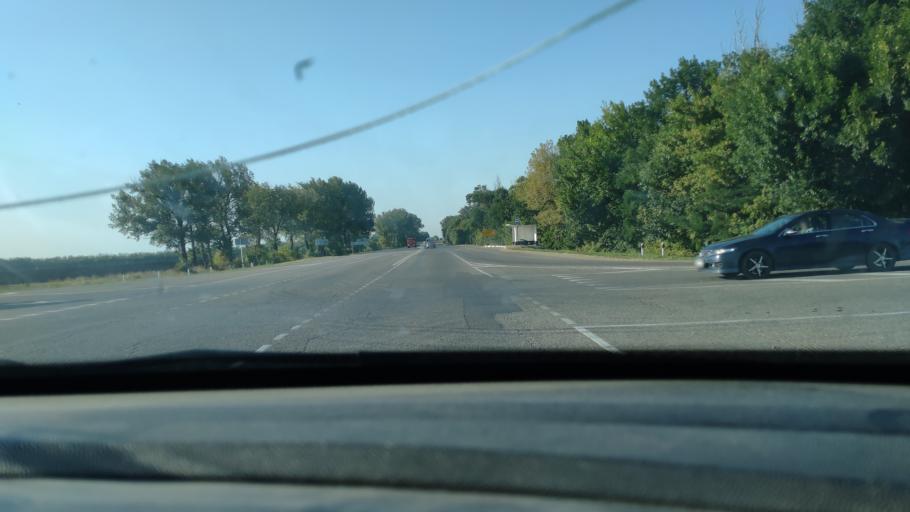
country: RU
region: Krasnodarskiy
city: Medvedovskaya
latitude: 45.4530
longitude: 38.9902
